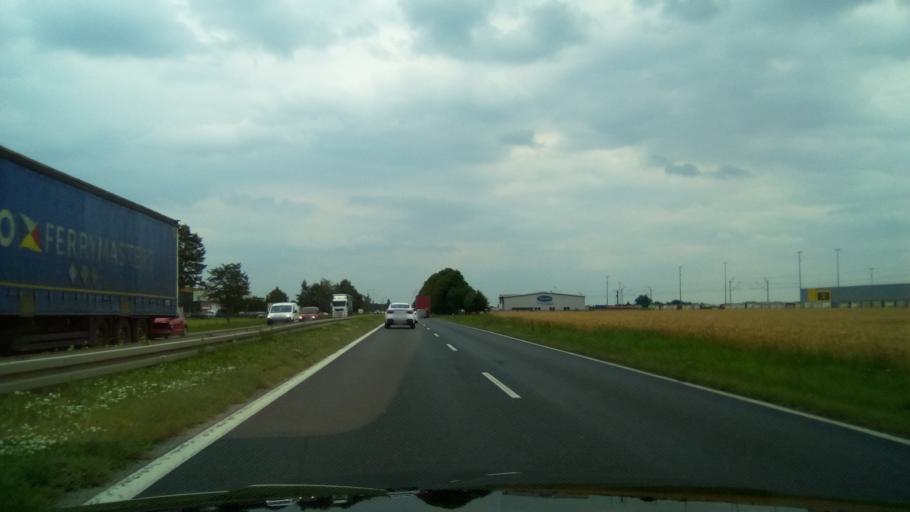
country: PL
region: Greater Poland Voivodeship
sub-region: Powiat poznanski
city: Swarzedz
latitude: 52.4007
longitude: 17.1319
